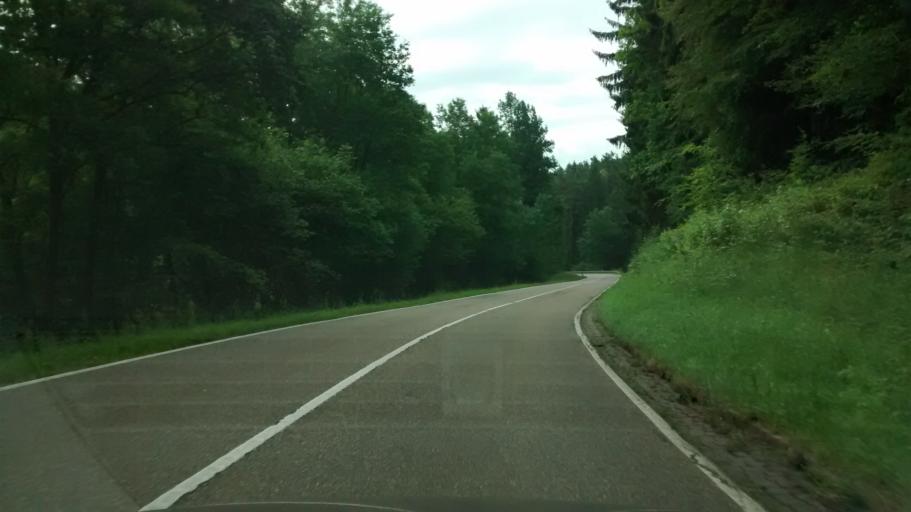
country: DE
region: Rheinland-Pfalz
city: Busenberg
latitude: 49.1245
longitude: 7.8500
